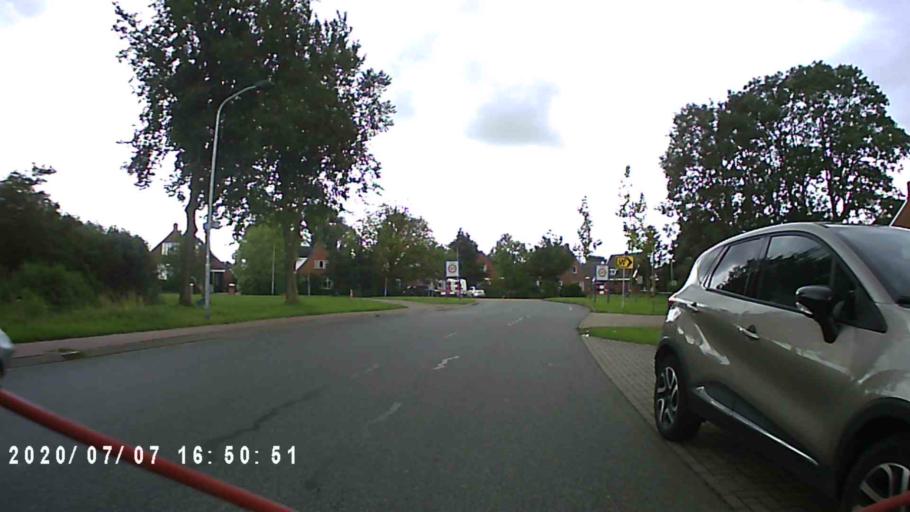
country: NL
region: Groningen
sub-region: Gemeente Winsum
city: Winsum
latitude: 53.3352
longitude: 6.5224
